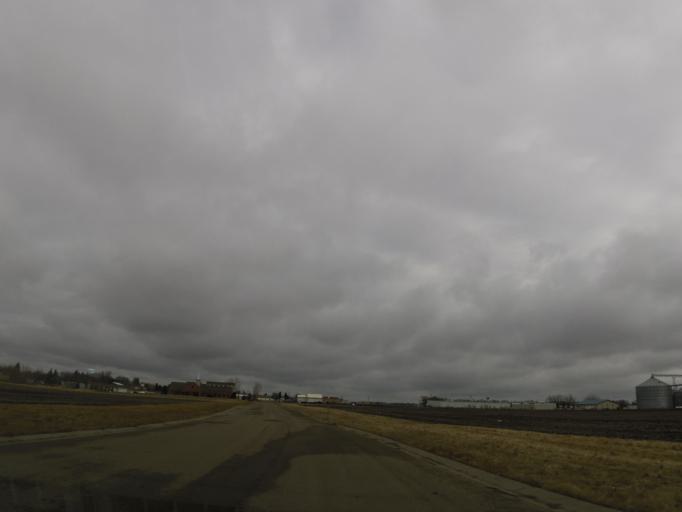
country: US
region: North Dakota
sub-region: Traill County
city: Mayville
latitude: 47.4935
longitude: -97.3130
